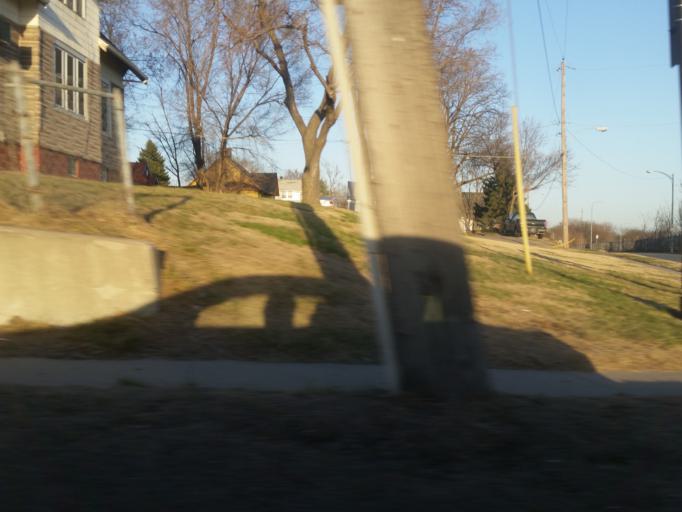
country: US
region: Nebraska
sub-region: Douglas County
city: Omaha
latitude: 41.2315
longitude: -95.9332
